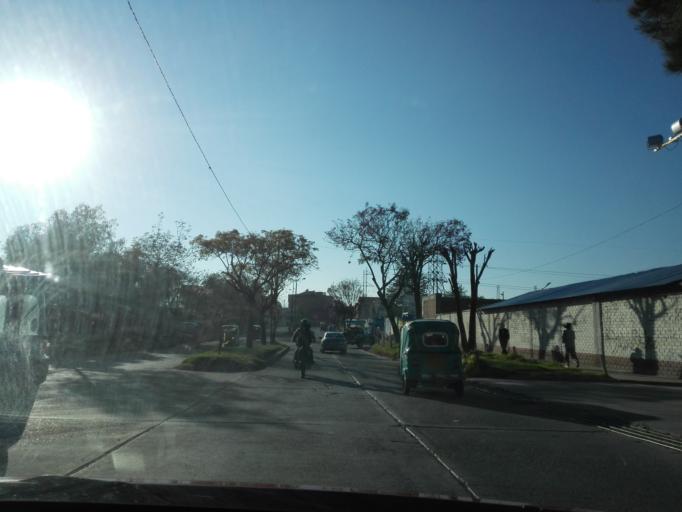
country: PE
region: Ayacucho
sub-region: Provincia de Huamanga
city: Ayacucho
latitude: -13.1500
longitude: -74.2213
